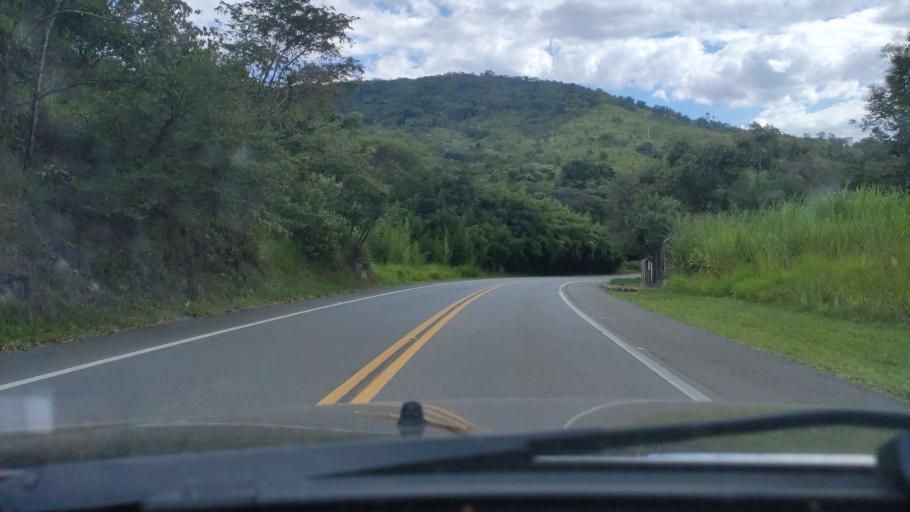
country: BR
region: Sao Paulo
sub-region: Aguas De Lindoia
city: Aguas de Lindoia
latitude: -22.4717
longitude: -46.7091
